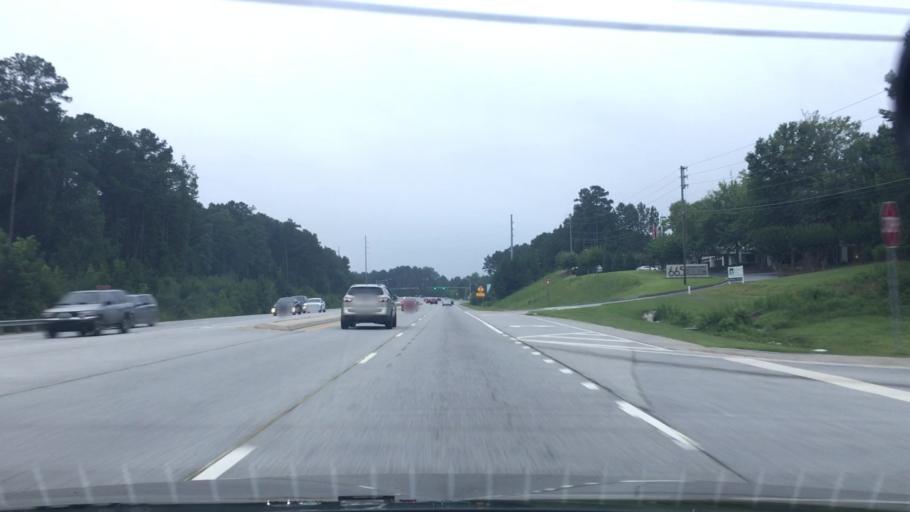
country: US
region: Georgia
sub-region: Fayette County
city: Peachtree City
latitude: 33.3619
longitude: -84.5624
